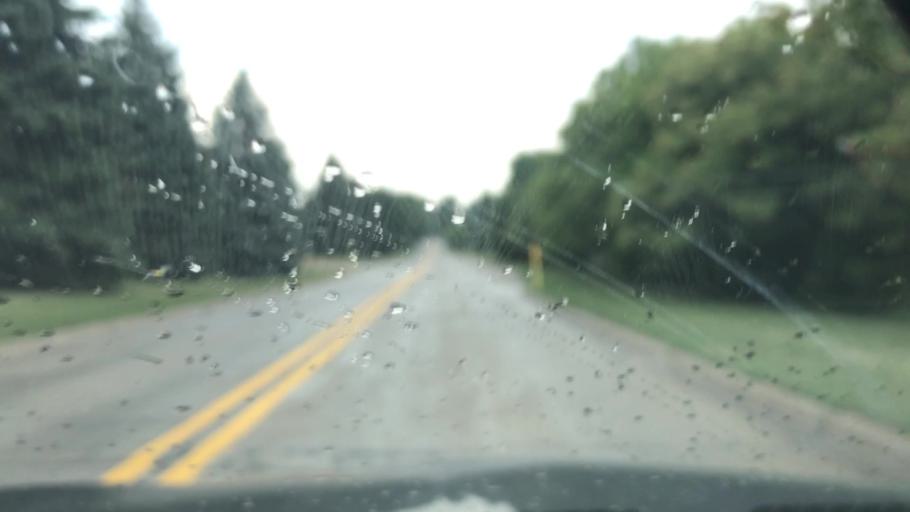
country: US
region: Michigan
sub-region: Oakland County
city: Farmington Hills
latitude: 42.5152
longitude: -83.4182
